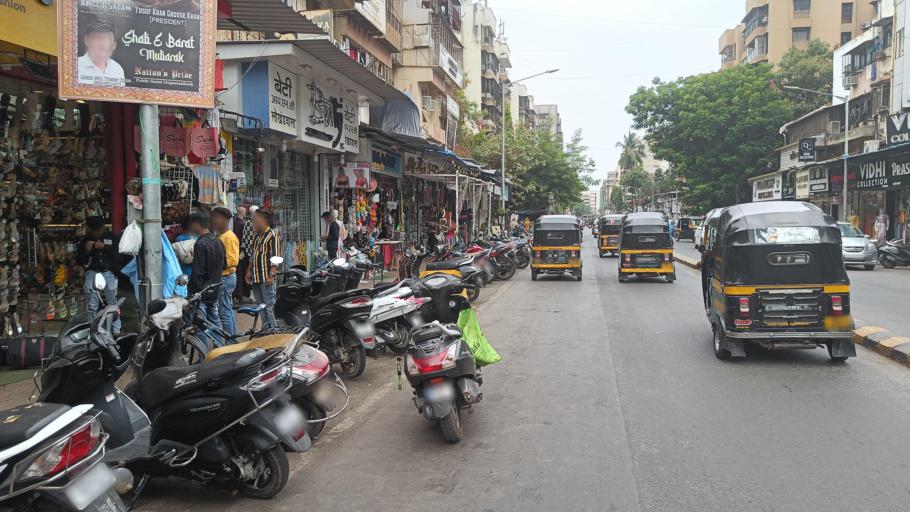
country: IN
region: Maharashtra
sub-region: Mumbai Suburban
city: Powai
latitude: 19.1418
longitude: 72.8253
